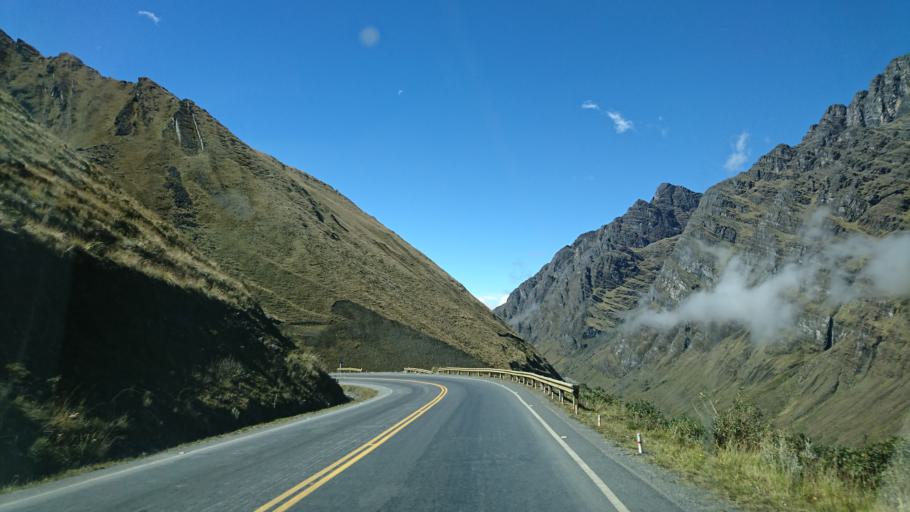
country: BO
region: La Paz
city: La Paz
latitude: -16.3292
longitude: -67.9578
